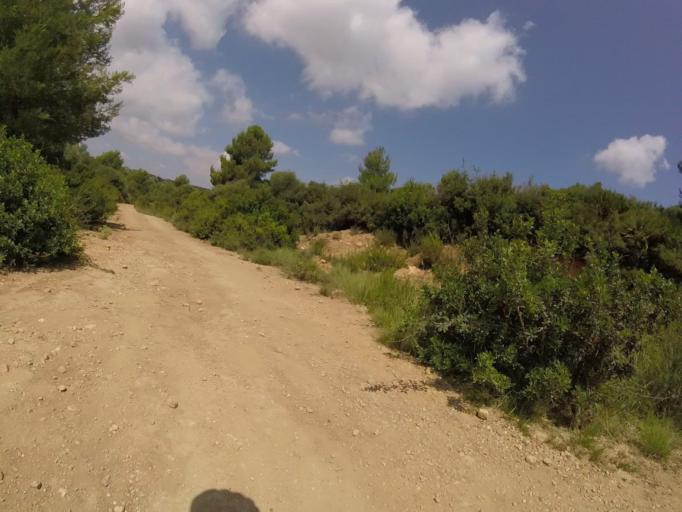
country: ES
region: Valencia
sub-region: Provincia de Castello
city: Torreblanca
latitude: 40.2039
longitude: 0.1409
